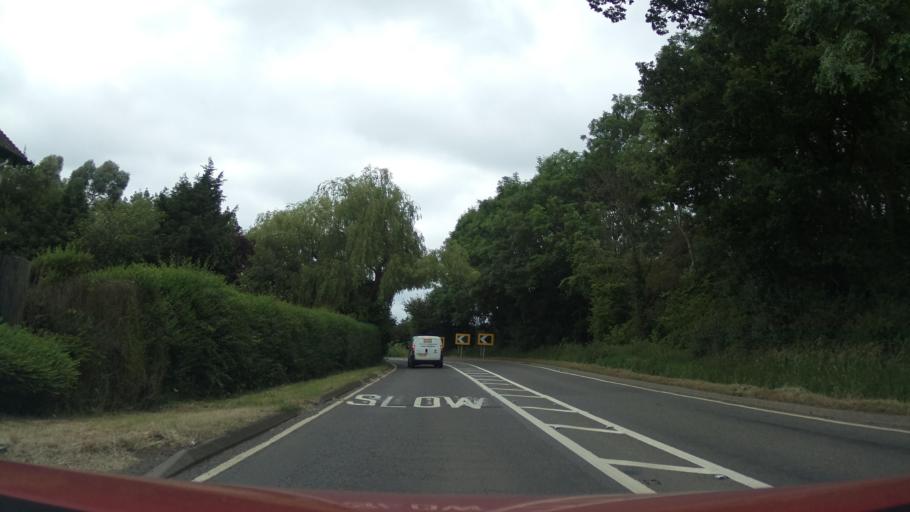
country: GB
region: England
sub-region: Leicestershire
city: Grimston
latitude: 52.7713
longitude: -0.9812
